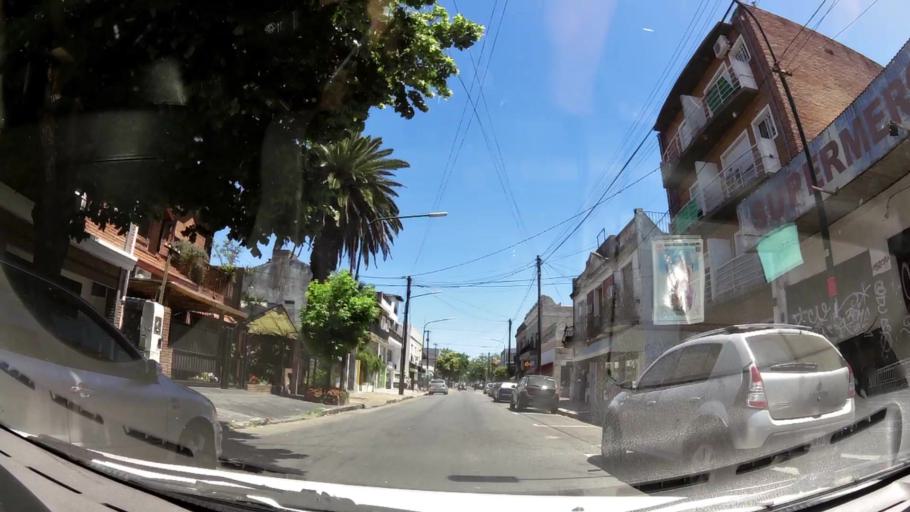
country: AR
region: Buenos Aires
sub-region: Partido de San Isidro
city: San Isidro
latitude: -34.4910
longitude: -58.5036
